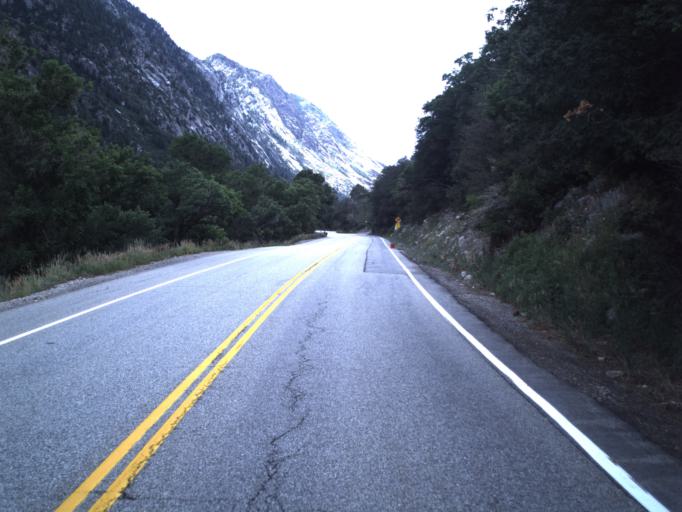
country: US
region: Utah
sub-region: Salt Lake County
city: Granite
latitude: 40.5719
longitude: -111.7351
